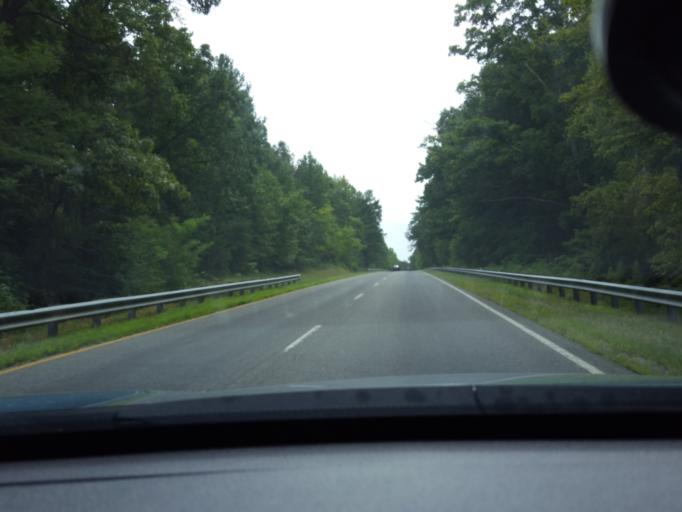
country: US
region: Virginia
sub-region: Caroline County
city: Bowling Green
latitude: 38.1295
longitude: -77.2407
